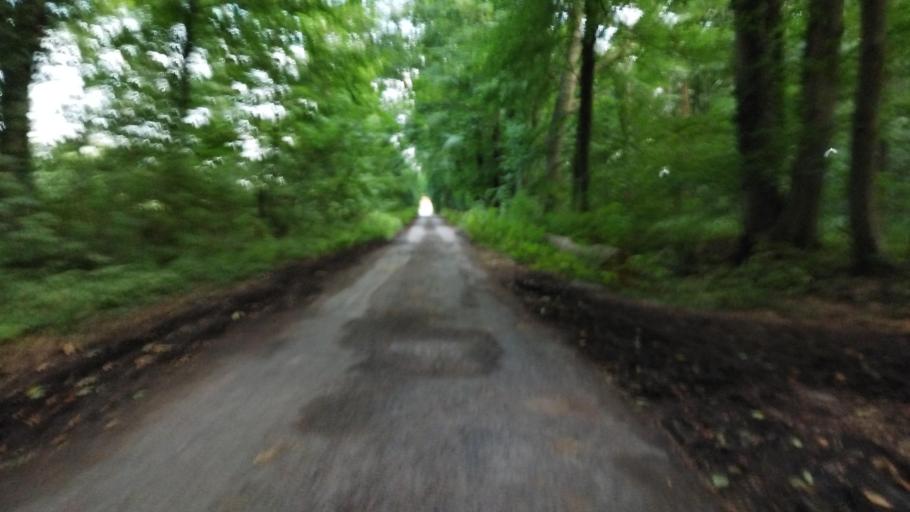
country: DE
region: Lower Saxony
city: Glandorf
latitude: 52.0897
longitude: 8.0346
